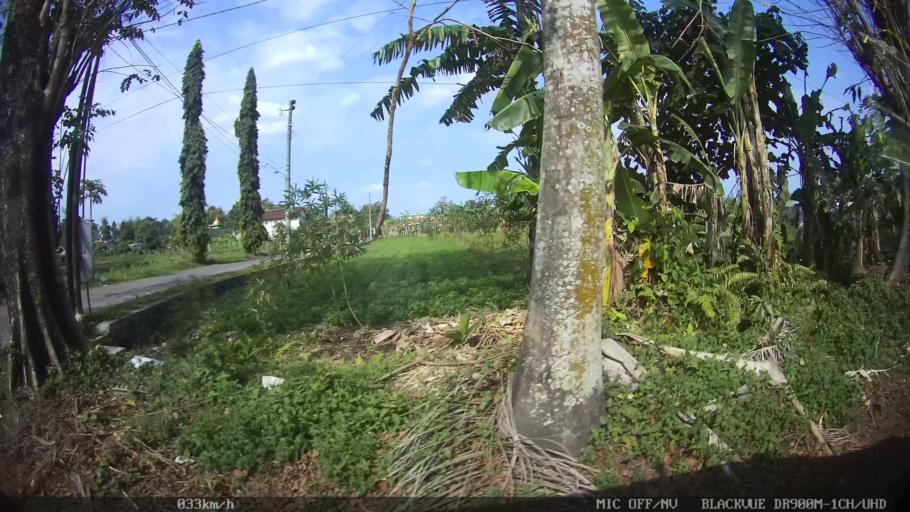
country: ID
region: Daerah Istimewa Yogyakarta
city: Depok
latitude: -7.7296
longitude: 110.4350
